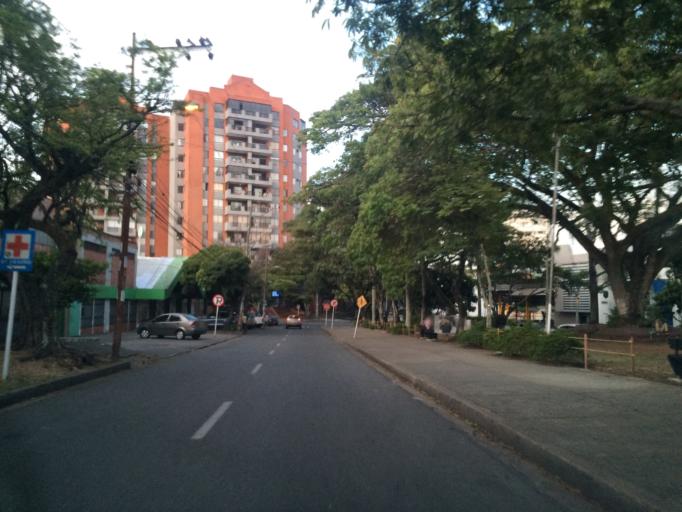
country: CO
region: Valle del Cauca
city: Cali
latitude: 3.4330
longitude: -76.5446
